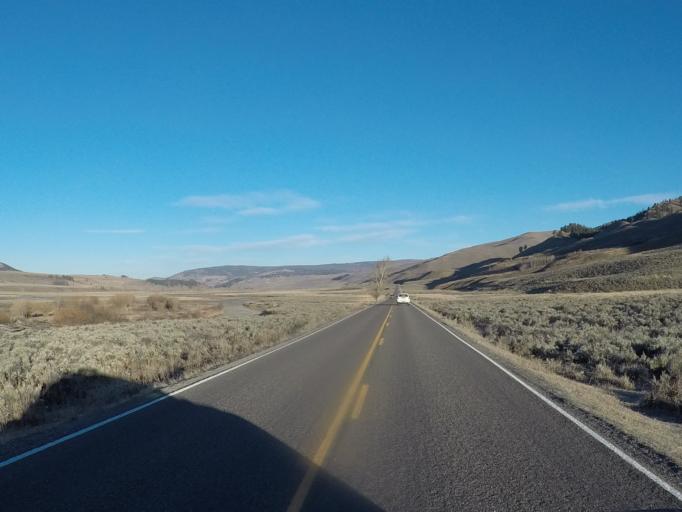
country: US
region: Montana
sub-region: Park County
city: Livingston
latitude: 44.8702
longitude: -110.1931
